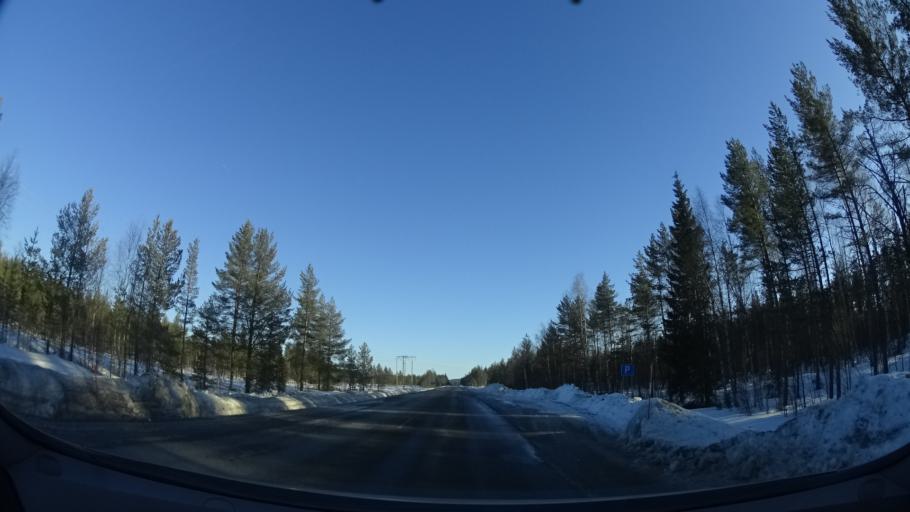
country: SE
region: Vaesterbotten
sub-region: Skelleftea Kommun
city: Langsele
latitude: 65.0516
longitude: 20.0610
